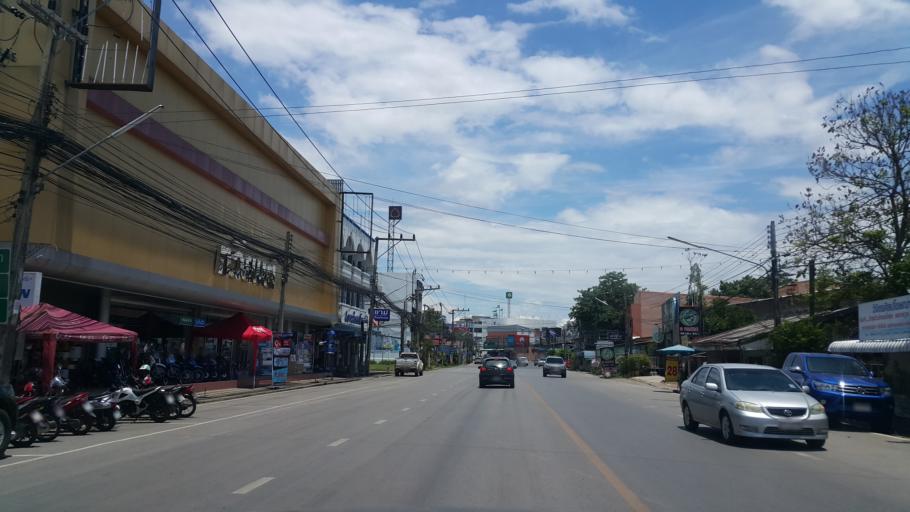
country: TH
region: Phayao
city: Phayao
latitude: 19.1715
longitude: 99.8956
